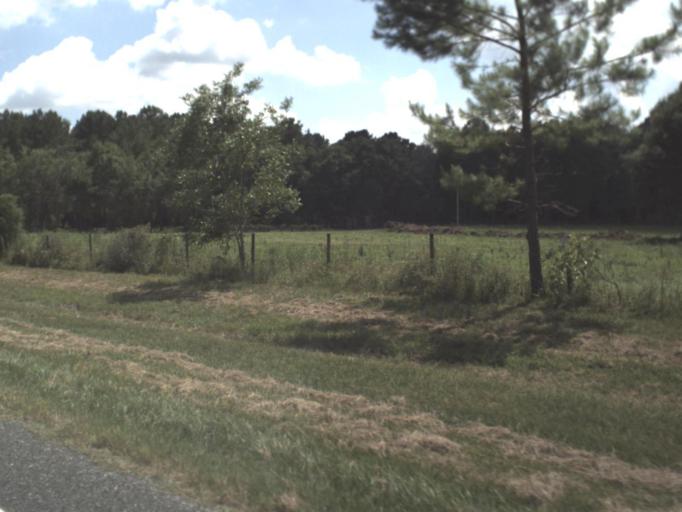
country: US
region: Florida
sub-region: Alachua County
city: High Springs
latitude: 29.9093
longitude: -82.6095
